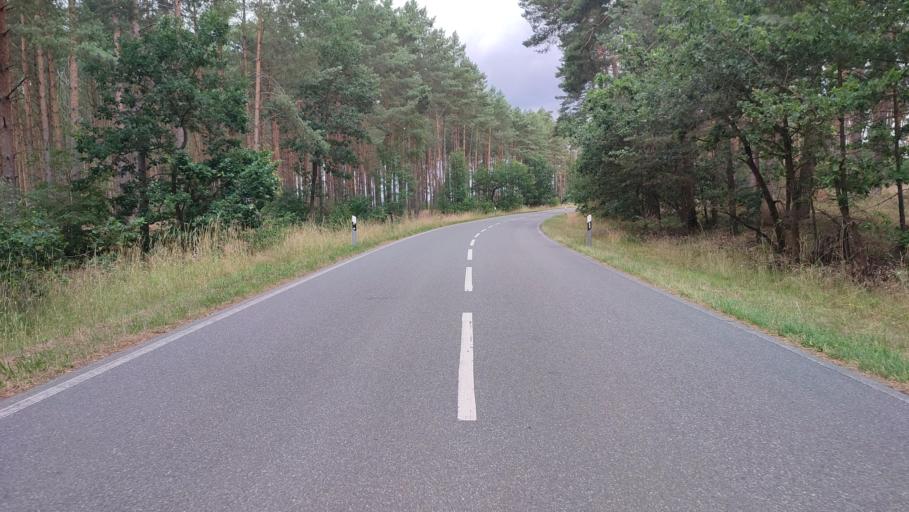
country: DE
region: Lower Saxony
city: Hitzacker
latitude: 53.1922
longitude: 11.1049
